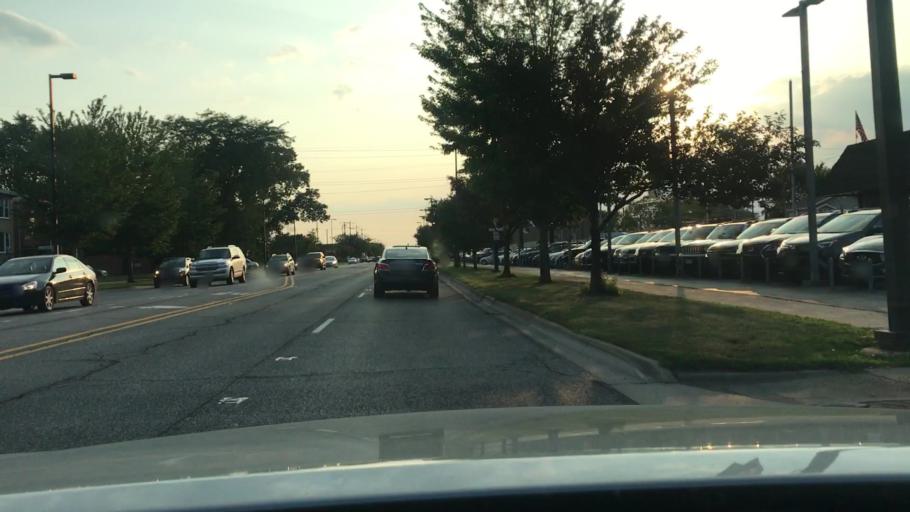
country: US
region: Illinois
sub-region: Cook County
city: Bridgeview
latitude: 41.7484
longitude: -87.7901
